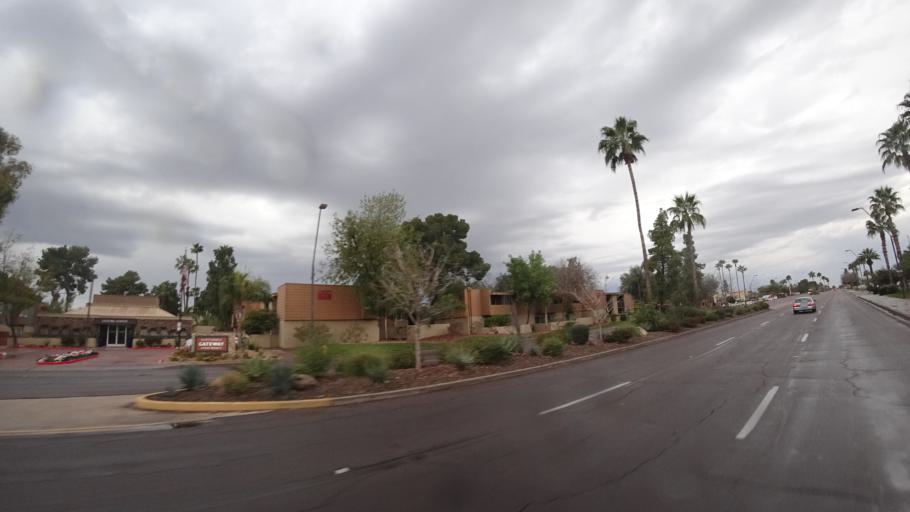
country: US
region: Arizona
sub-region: Maricopa County
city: Tempe
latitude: 33.4521
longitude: -111.9263
